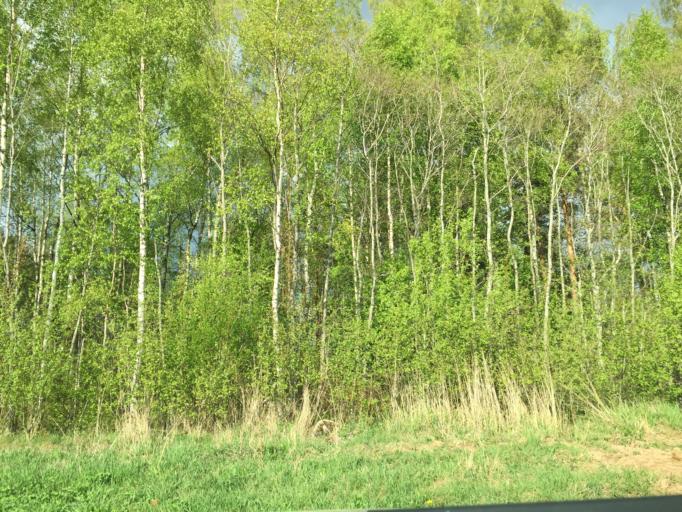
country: LV
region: Limbazu Rajons
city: Limbazi
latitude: 57.3782
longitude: 24.7752
